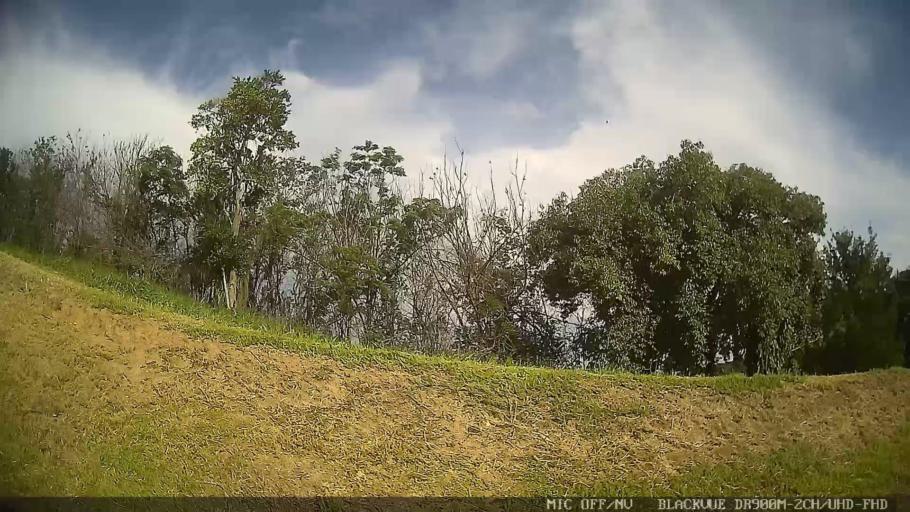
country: BR
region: Sao Paulo
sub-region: Tiete
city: Tiete
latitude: -23.1091
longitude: -47.6954
